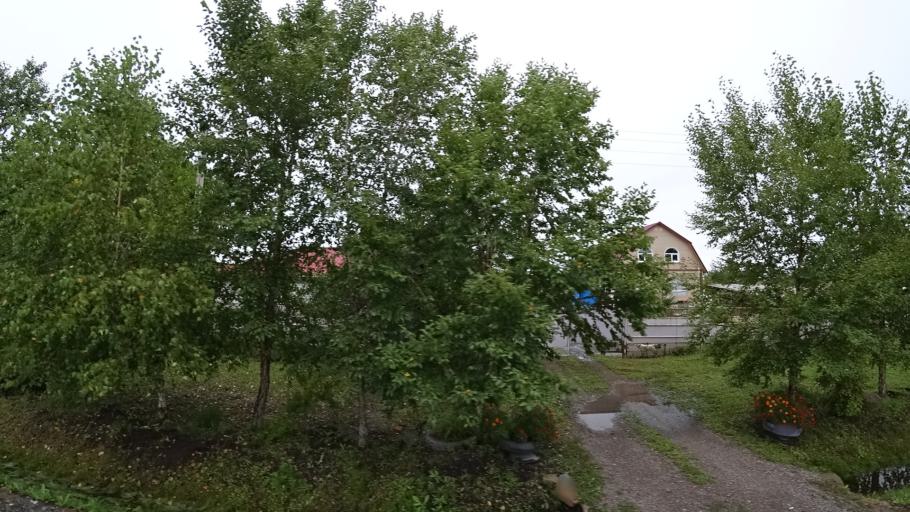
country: RU
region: Primorskiy
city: Monastyrishche
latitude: 44.1913
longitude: 132.4868
